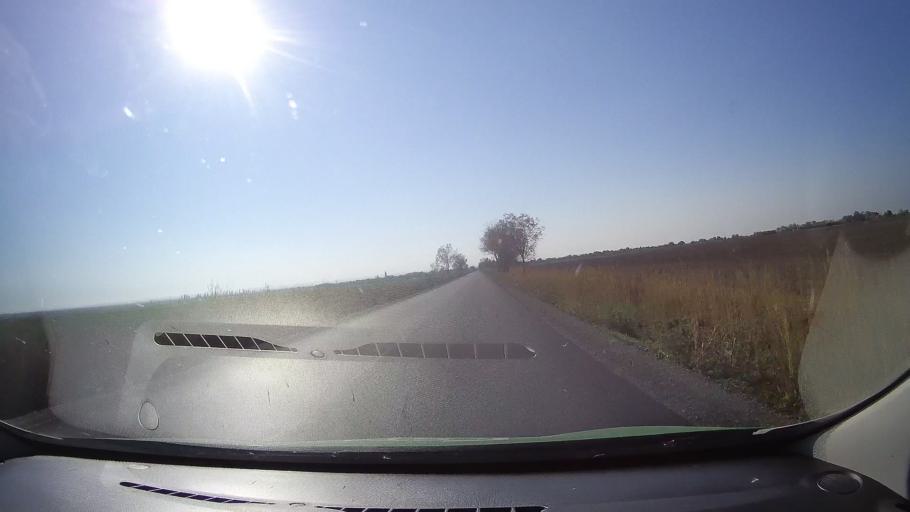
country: RO
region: Satu Mare
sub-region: Comuna Tiream
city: Tiream
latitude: 47.6279
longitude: 22.4676
